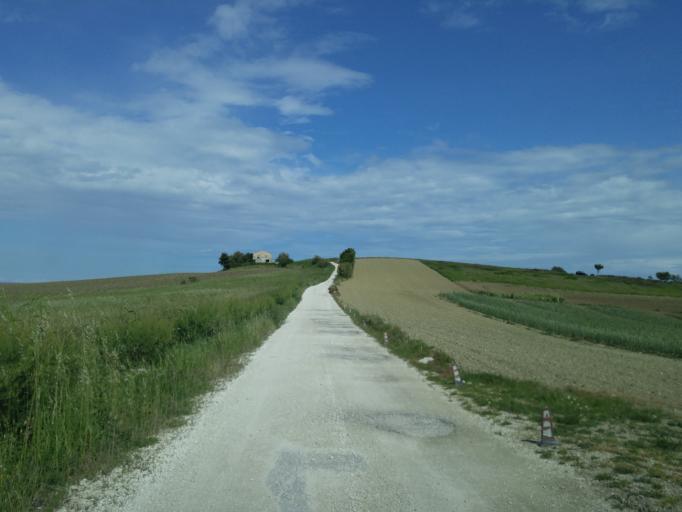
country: IT
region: The Marches
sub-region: Provincia di Pesaro e Urbino
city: San Costanzo
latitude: 43.7974
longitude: 13.0490
